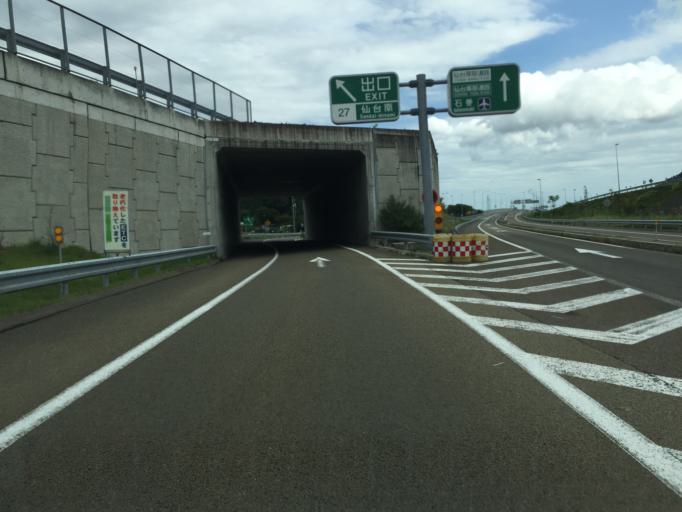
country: JP
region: Miyagi
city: Sendai
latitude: 38.2155
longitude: 140.8042
